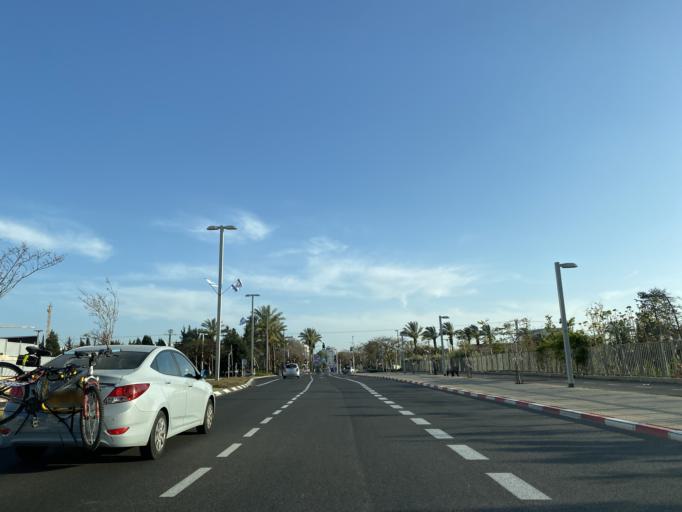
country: IL
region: Tel Aviv
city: Herzliyya
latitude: 32.1723
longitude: 34.8291
